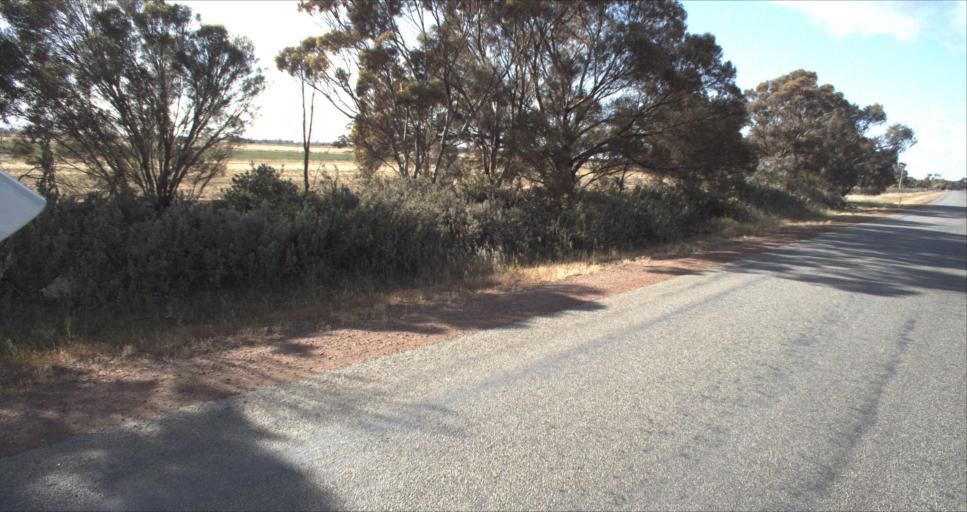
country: AU
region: New South Wales
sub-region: Leeton
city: Leeton
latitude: -34.5084
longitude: 146.3927
